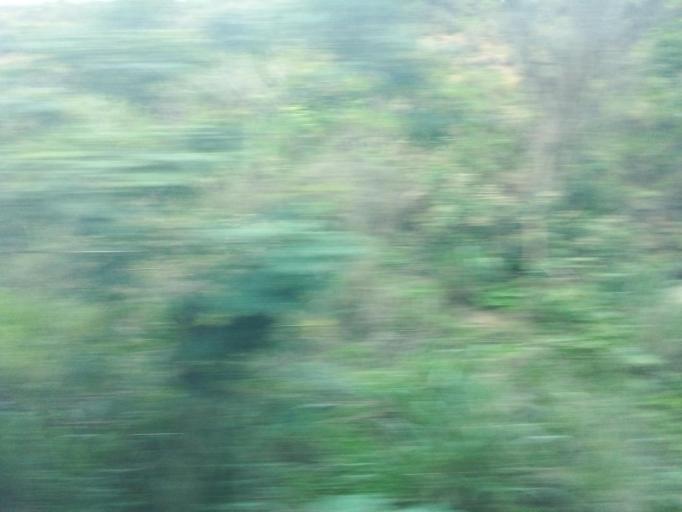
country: BR
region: Minas Gerais
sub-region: Belo Oriente
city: Belo Oriente
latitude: -19.2216
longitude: -42.2999
